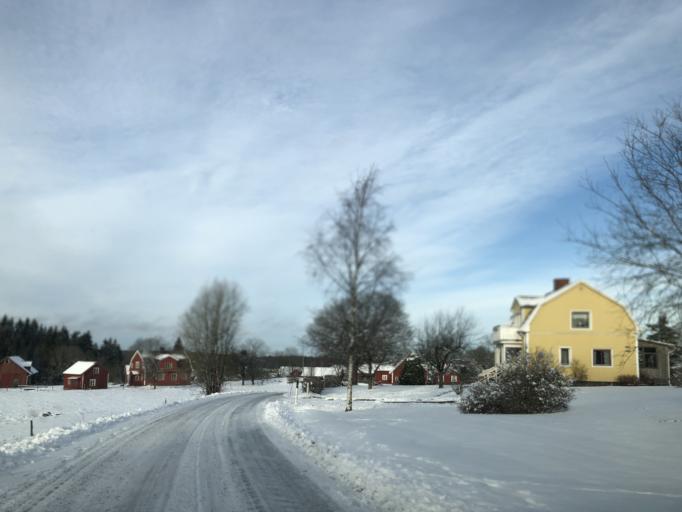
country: SE
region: Vaestra Goetaland
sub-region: Ulricehamns Kommun
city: Ulricehamn
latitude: 57.7802
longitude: 13.5241
